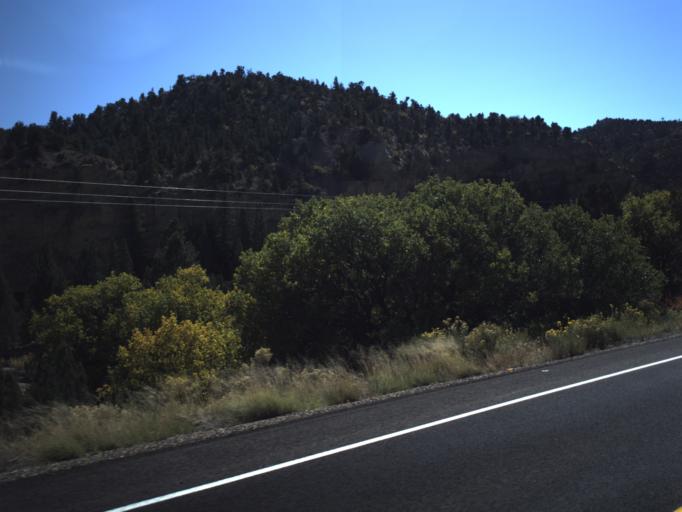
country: US
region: Utah
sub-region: Garfield County
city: Panguitch
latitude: 37.6112
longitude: -111.8981
